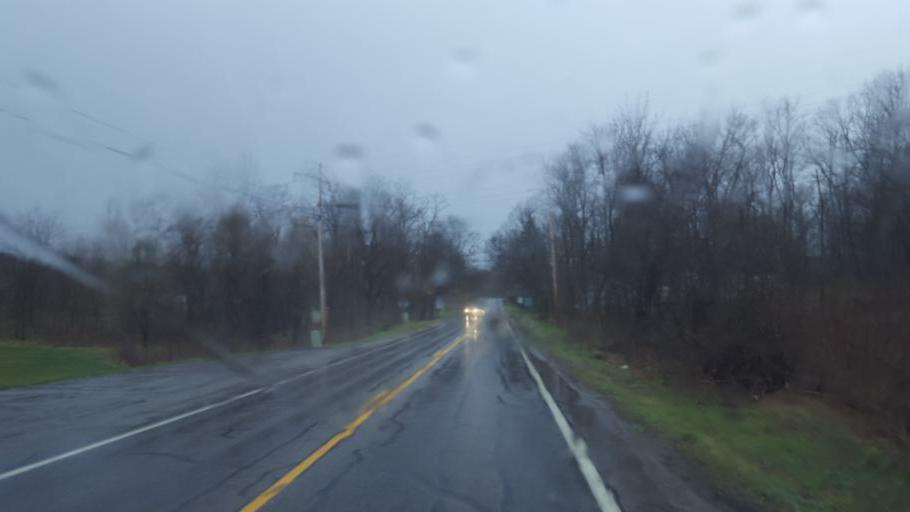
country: US
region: Ohio
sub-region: Delaware County
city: Powell
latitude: 40.1382
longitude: -83.0380
